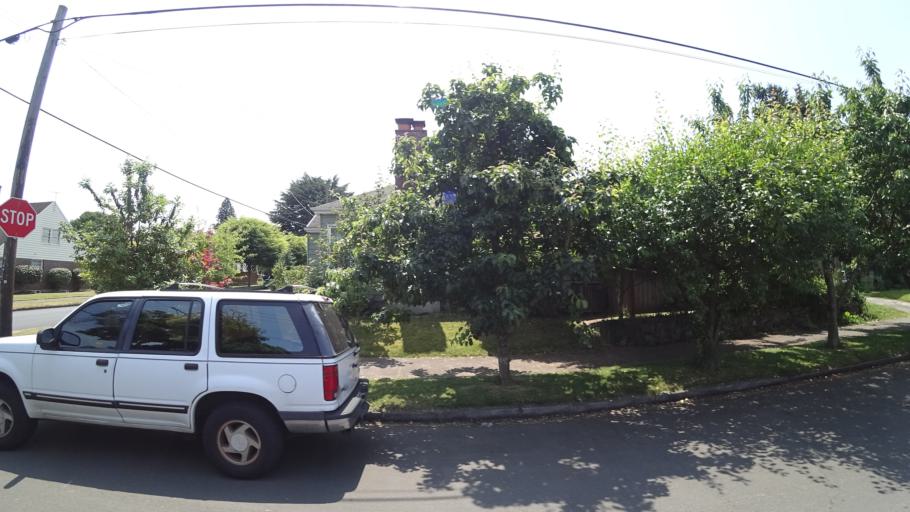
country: US
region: Oregon
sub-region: Multnomah County
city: Portland
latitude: 45.5817
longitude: -122.6850
